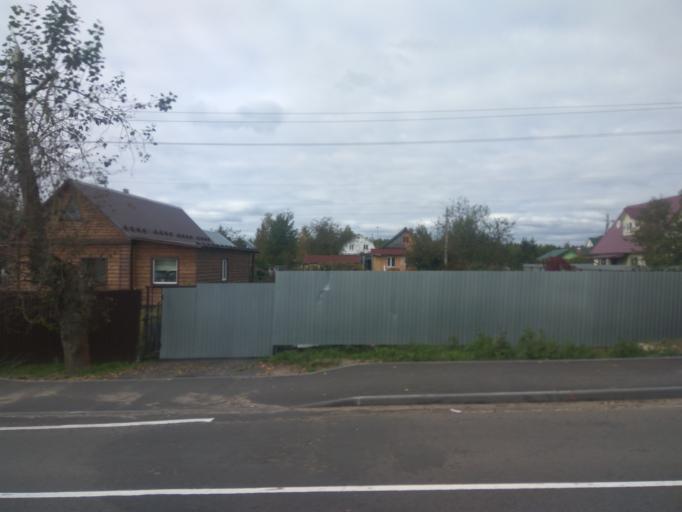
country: RU
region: Moskovskaya
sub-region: Shchelkovskiy Rayon
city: Grebnevo
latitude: 55.9945
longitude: 38.1282
